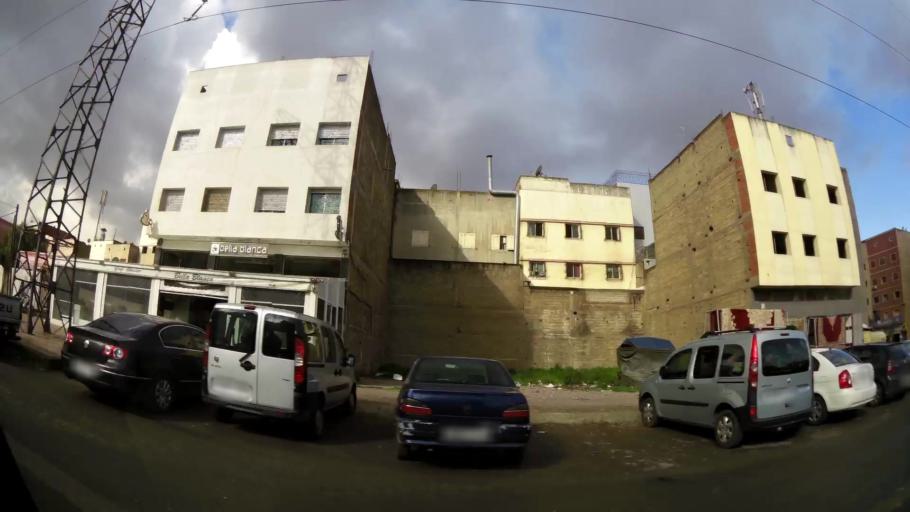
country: MA
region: Grand Casablanca
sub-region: Mediouna
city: Tit Mellil
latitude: 33.5871
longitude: -7.5239
